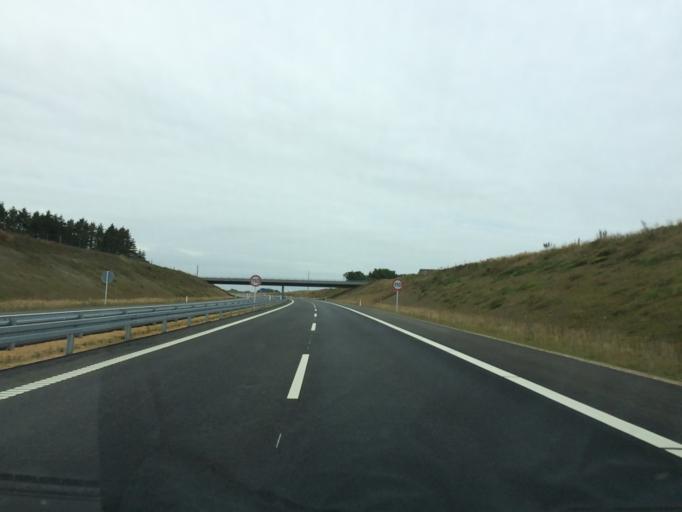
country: DK
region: Central Jutland
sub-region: Herning Kommune
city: Snejbjerg
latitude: 56.1363
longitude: 8.8697
